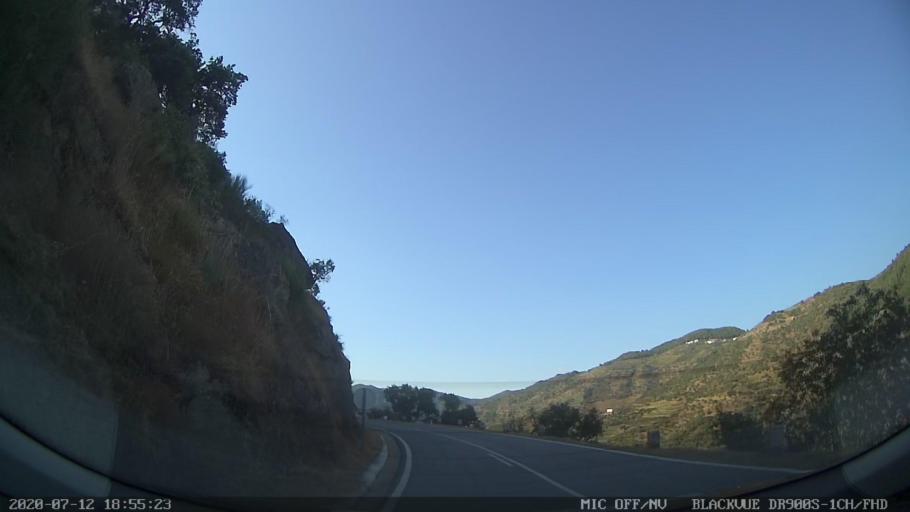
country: PT
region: Viseu
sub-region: Sao Joao da Pesqueira
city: Sao Joao da Pesqueira
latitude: 41.2227
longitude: -7.4231
